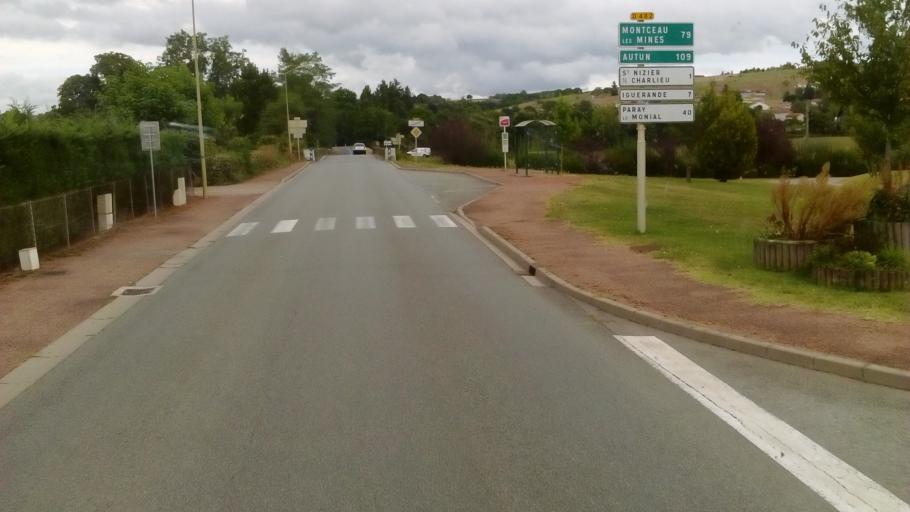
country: FR
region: Rhone-Alpes
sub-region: Departement de la Loire
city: Pouilly-sous-Charlieu
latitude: 46.1502
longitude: 4.1088
